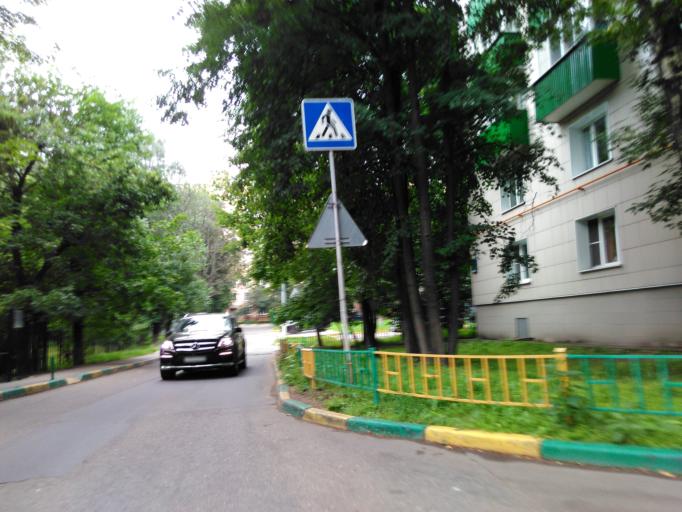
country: RU
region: Moskovskaya
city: Semenovskoye
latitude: 55.6745
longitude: 37.5366
